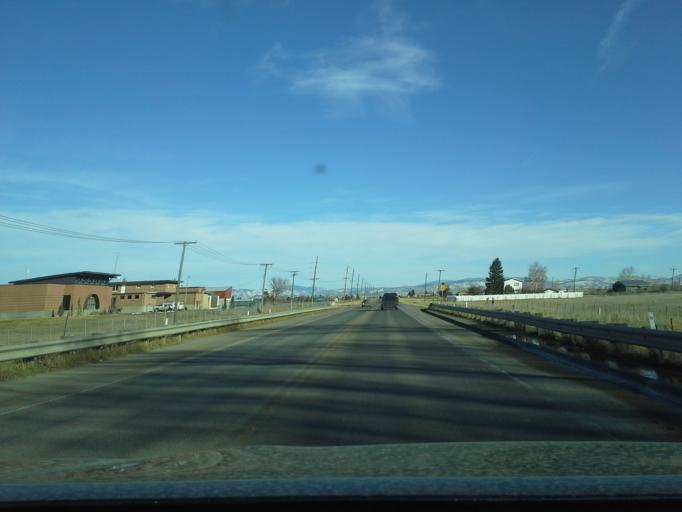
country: US
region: Montana
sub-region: Lewis and Clark County
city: Helena Valley Southeast
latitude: 46.6169
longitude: -111.9604
